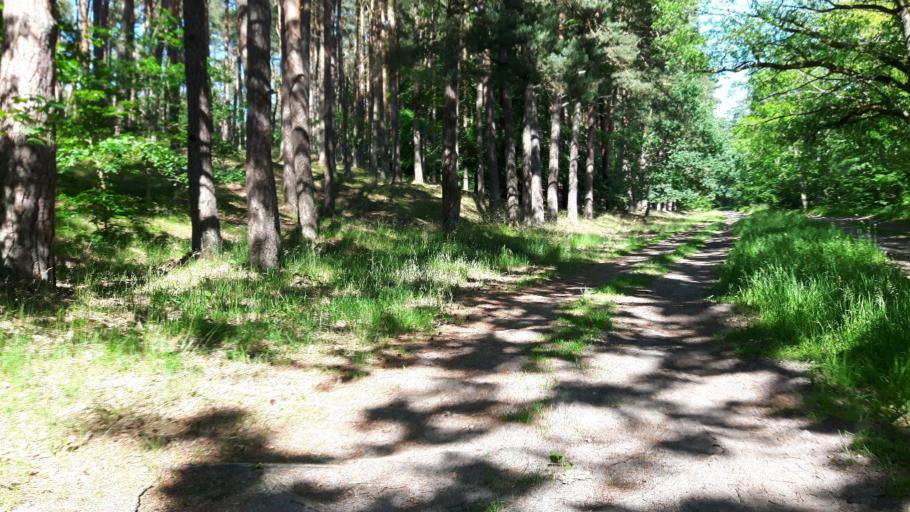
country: PL
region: Pomeranian Voivodeship
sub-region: Powiat leborski
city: Leba
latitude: 54.6942
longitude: 17.4670
